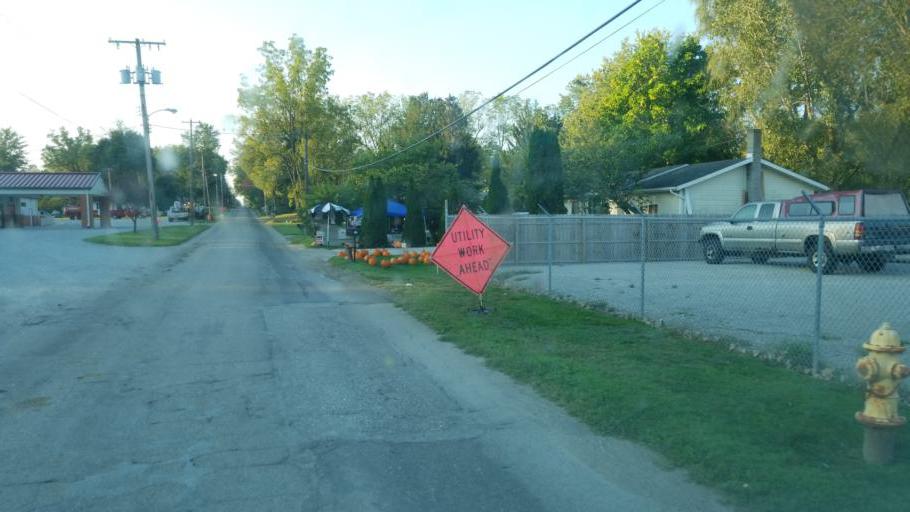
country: US
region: Indiana
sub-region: LaGrange County
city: Lagrange
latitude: 41.6409
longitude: -85.4249
